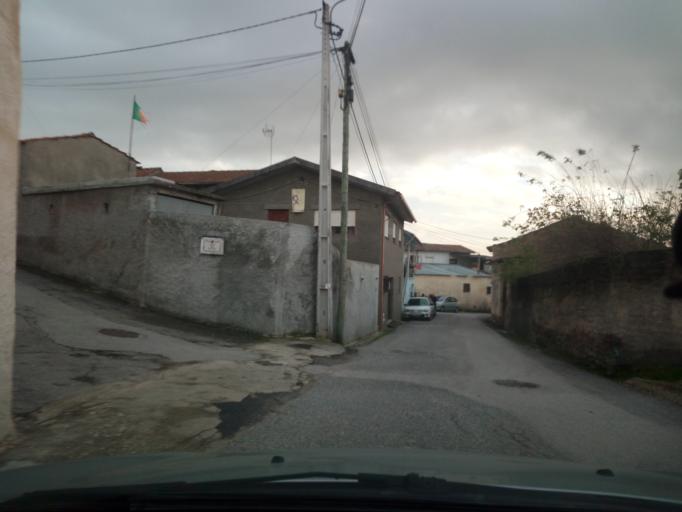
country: PT
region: Aveiro
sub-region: Oliveira do Bairro
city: Oliveira do Bairro
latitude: 40.5435
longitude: -8.4881
